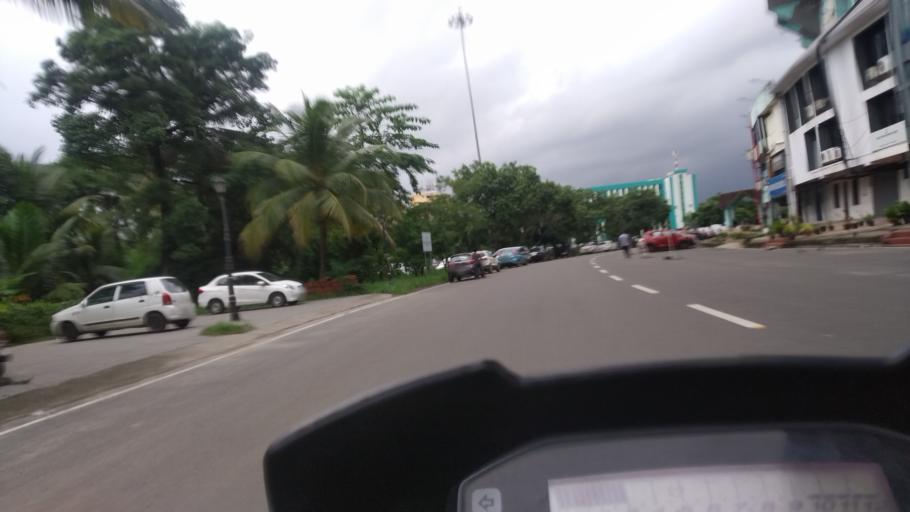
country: IN
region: Kerala
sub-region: Ernakulam
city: Cochin
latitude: 9.9966
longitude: 76.2999
